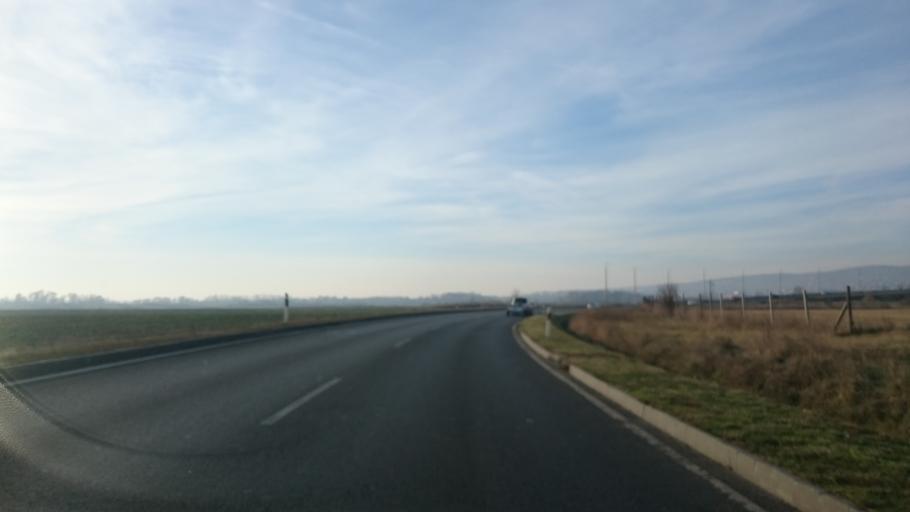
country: HU
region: Baranya
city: Pellerd
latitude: 46.0550
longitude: 18.1792
